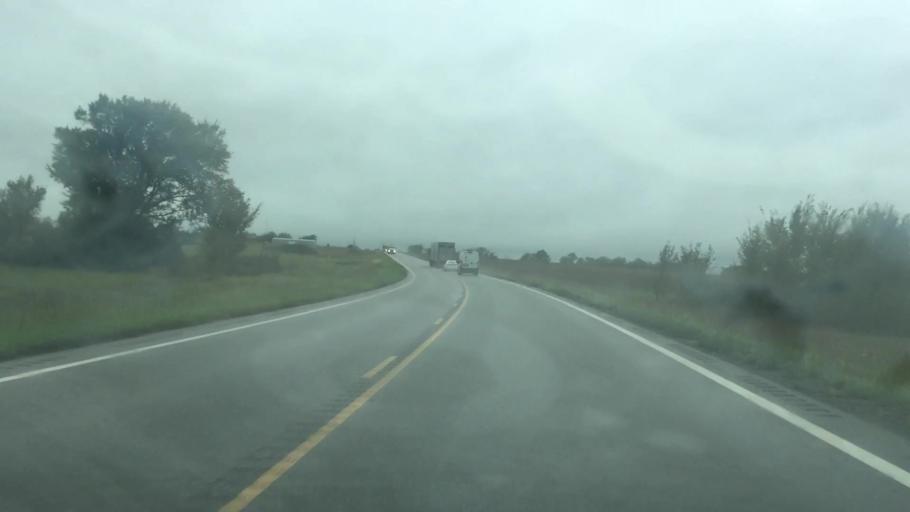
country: US
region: Kansas
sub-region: Anderson County
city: Garnett
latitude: 38.1602
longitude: -95.3096
